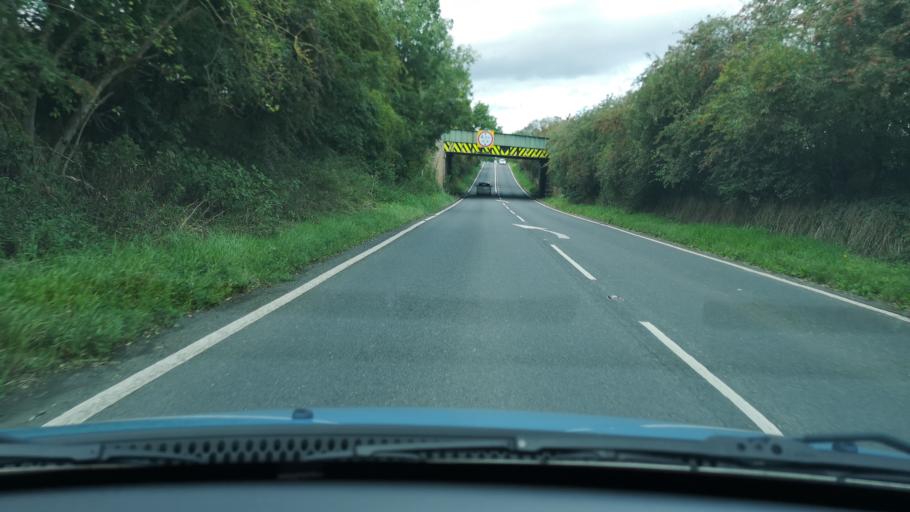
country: GB
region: England
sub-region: City and Borough of Wakefield
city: Badsworth
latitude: 53.6295
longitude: -1.3192
